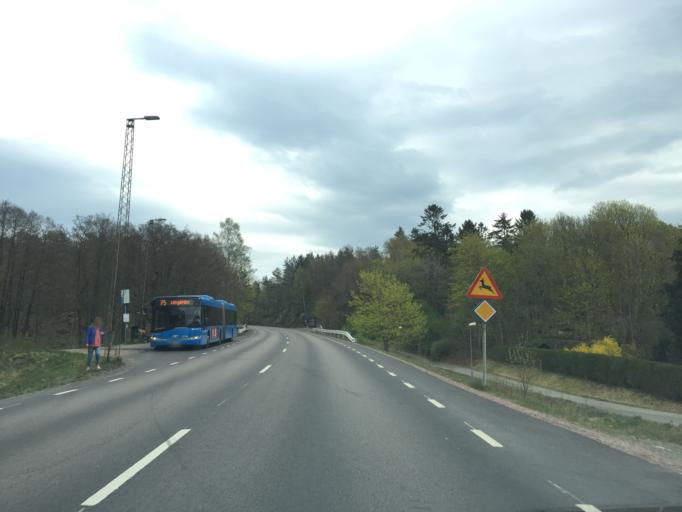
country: SE
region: Vaestra Goetaland
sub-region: Goteborg
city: Loevgaerdet
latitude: 57.8086
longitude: 12.0464
